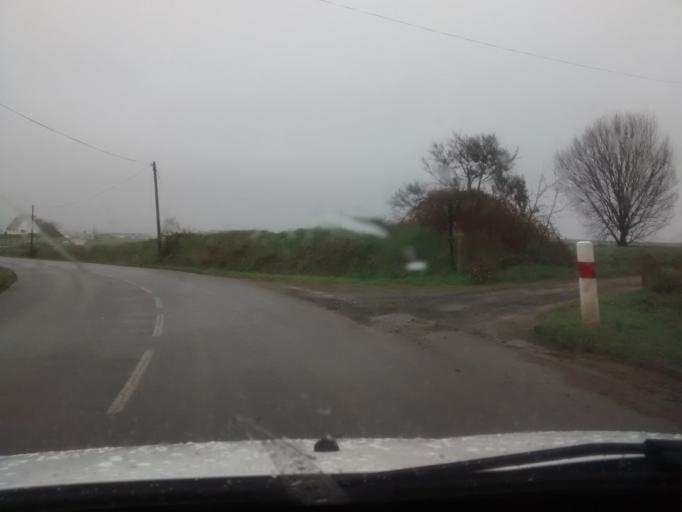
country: FR
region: Brittany
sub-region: Departement des Cotes-d'Armor
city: Penvenan
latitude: 48.7950
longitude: -3.2934
